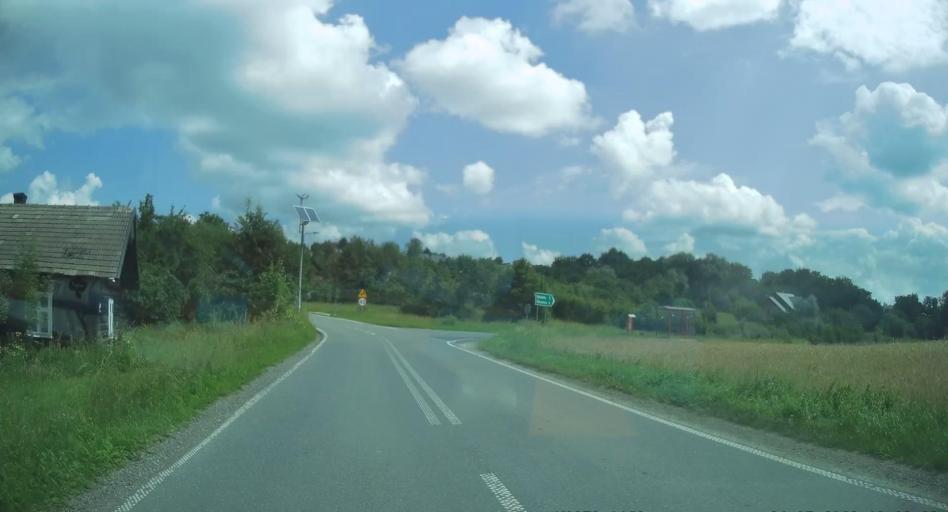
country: PL
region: Lesser Poland Voivodeship
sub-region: Powiat nowosadecki
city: Korzenna
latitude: 49.7030
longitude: 20.7621
